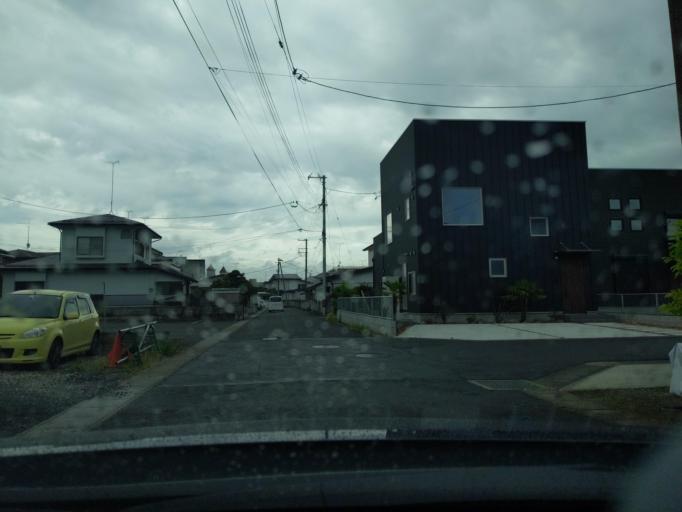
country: JP
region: Fukushima
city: Koriyama
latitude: 37.3677
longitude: 140.3576
